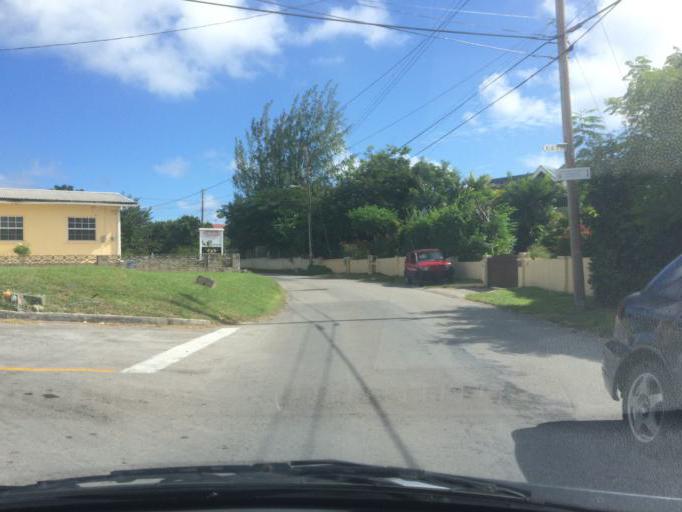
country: BB
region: Christ Church
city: Oistins
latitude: 13.0536
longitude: -59.5349
